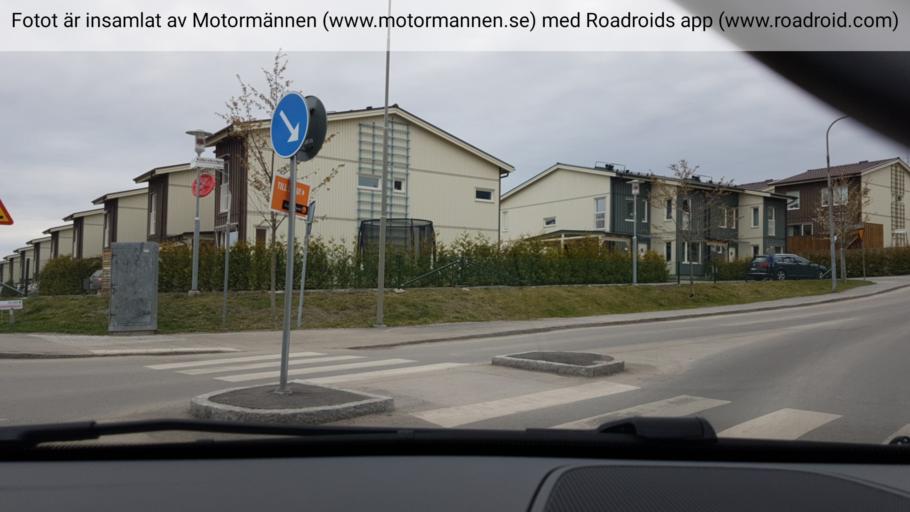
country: SE
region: Stockholm
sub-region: Jarfalla Kommun
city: Jakobsberg
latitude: 59.3771
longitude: 17.8155
